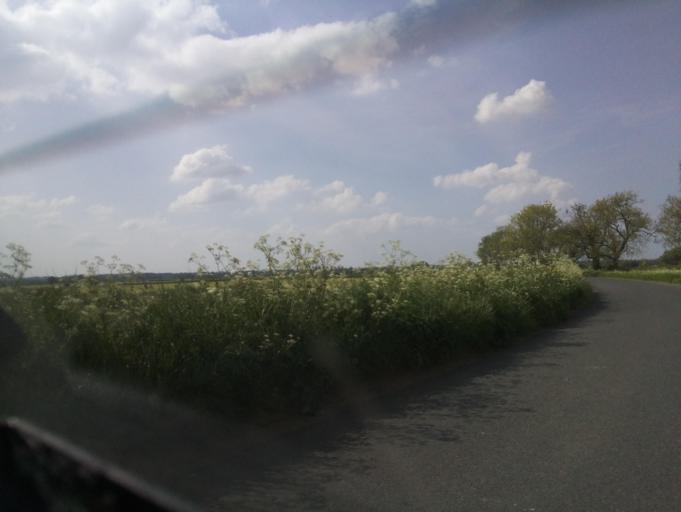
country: GB
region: England
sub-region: Wiltshire
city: Luckington
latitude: 51.5819
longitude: -2.2208
